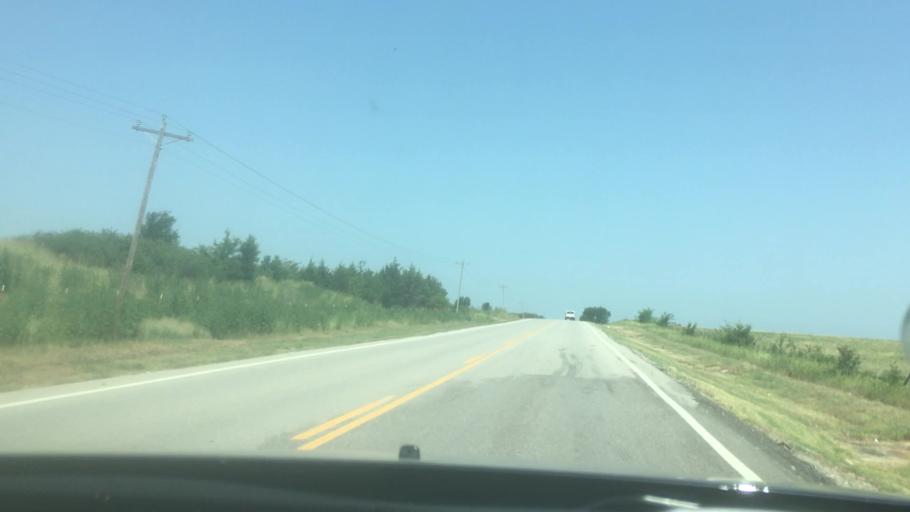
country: US
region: Oklahoma
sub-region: Bryan County
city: Durant
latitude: 34.1523
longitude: -96.3814
